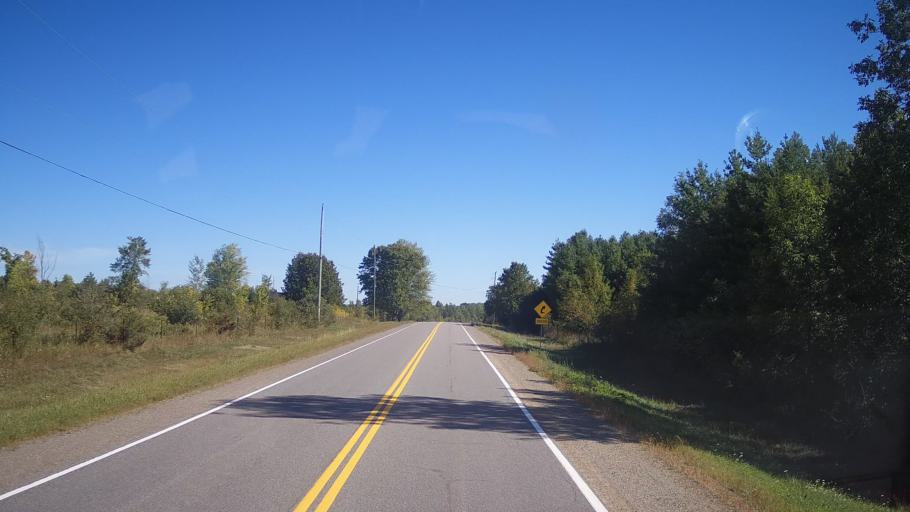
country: CA
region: Ontario
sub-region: Lanark County
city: Smiths Falls
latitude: 44.8080
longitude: -75.9687
